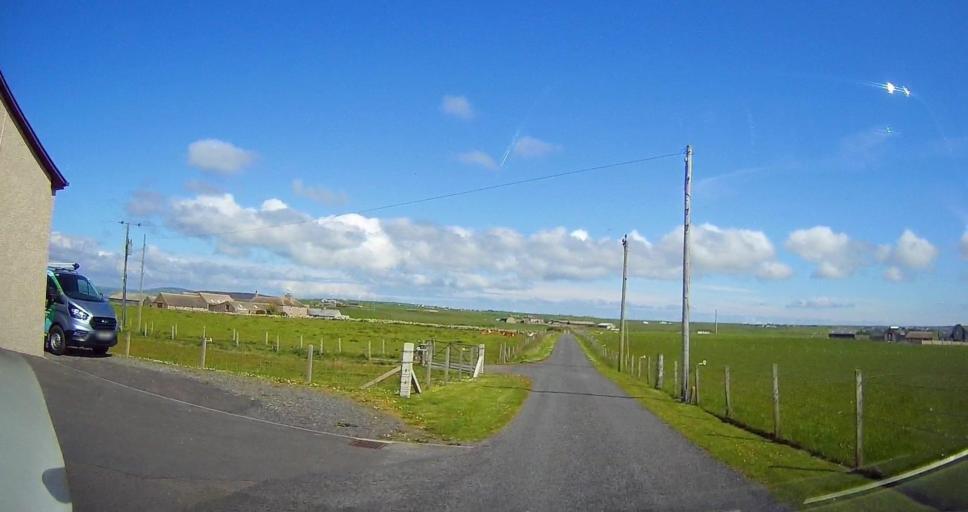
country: GB
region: Scotland
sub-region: Orkney Islands
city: Kirkwall
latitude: 58.8978
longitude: -2.9293
